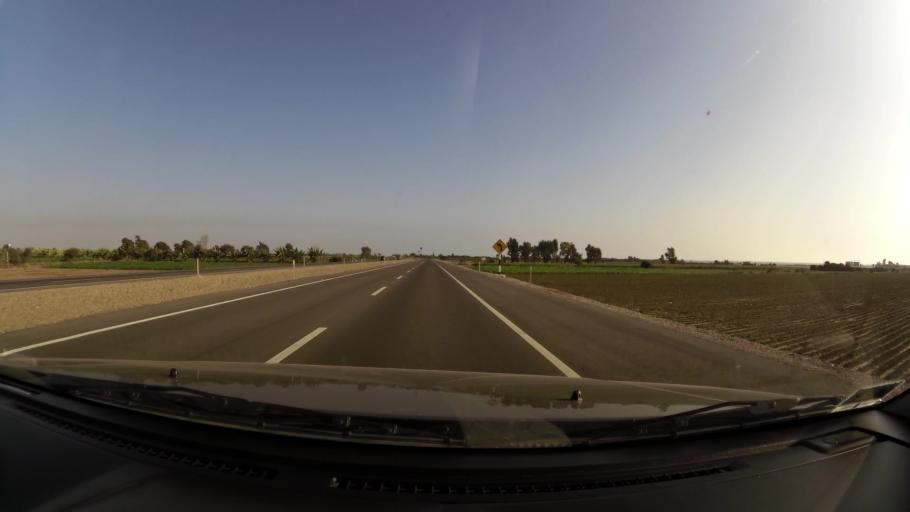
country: PE
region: Ica
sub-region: Provincia de Chincha
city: Chincha Baja
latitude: -13.4713
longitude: -76.1826
